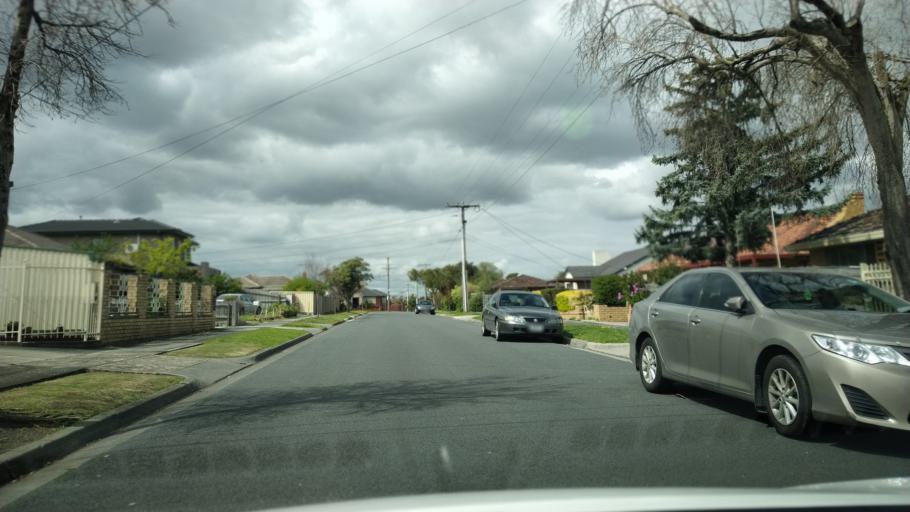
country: AU
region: Victoria
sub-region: Greater Dandenong
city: Noble Park
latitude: -37.9746
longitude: 145.1771
